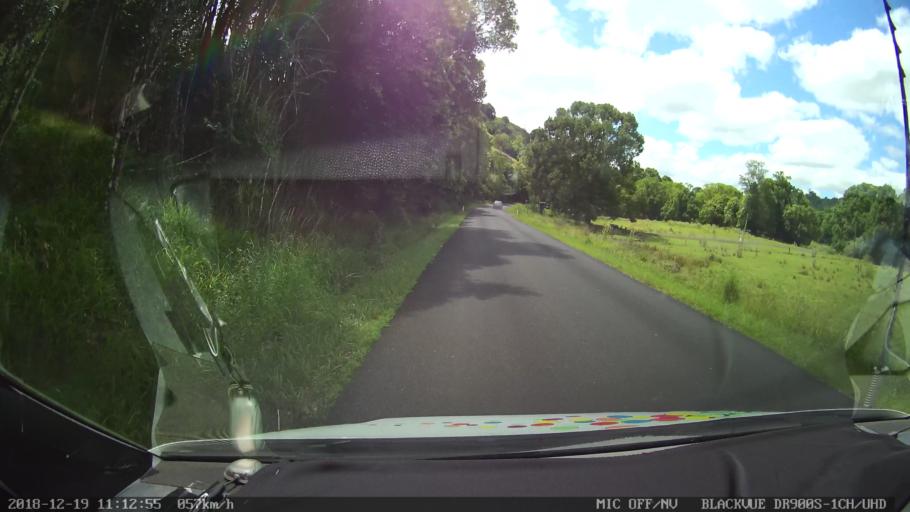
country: AU
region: New South Wales
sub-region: Lismore Municipality
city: Nimbin
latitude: -28.6525
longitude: 153.2613
